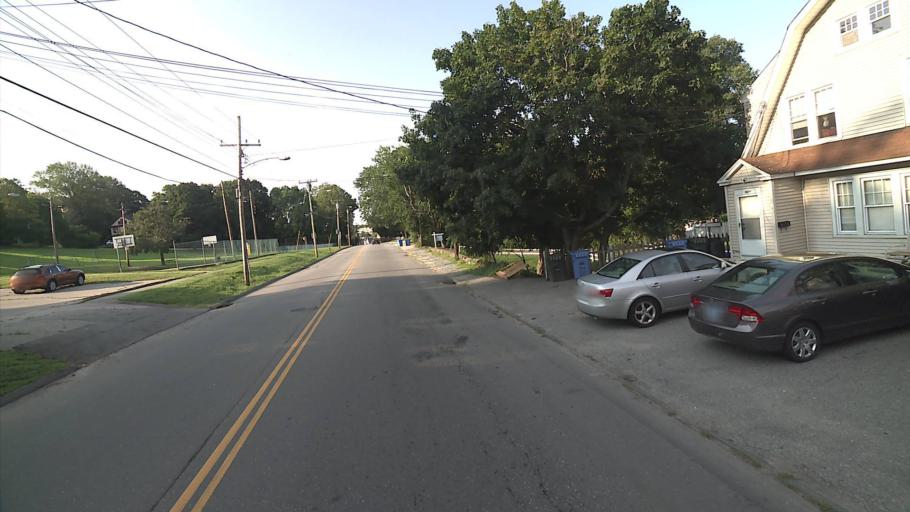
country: US
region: Connecticut
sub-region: New London County
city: Norwich
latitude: 41.5311
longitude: -72.0826
